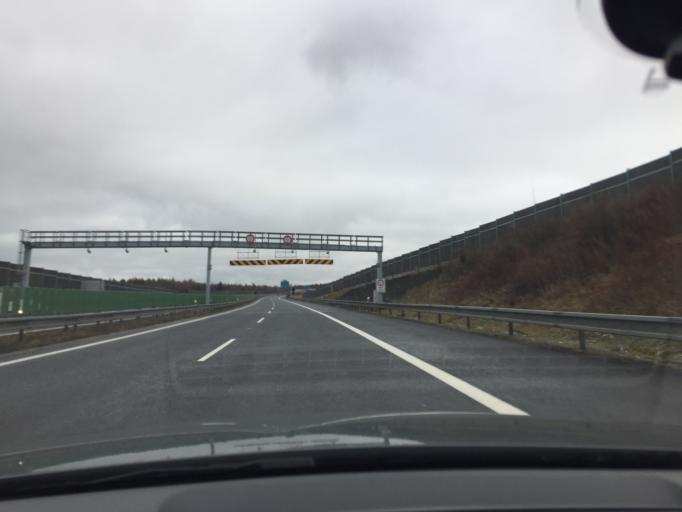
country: CZ
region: Ustecky
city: Chlumec
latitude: 50.7706
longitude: 13.9571
